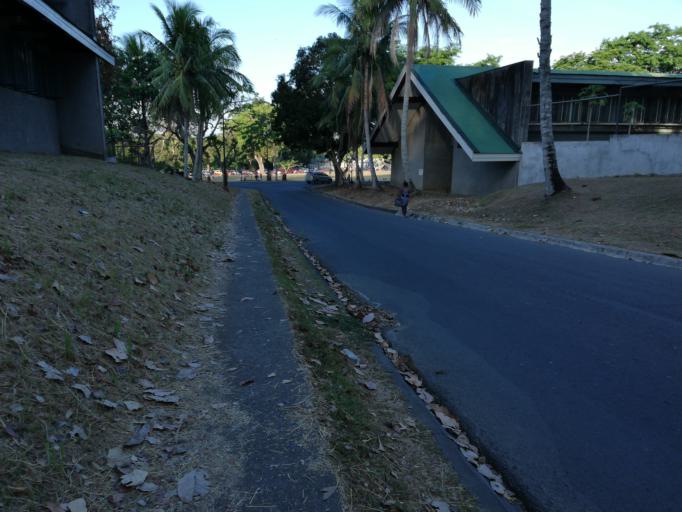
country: PH
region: Calabarzon
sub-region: Province of Laguna
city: Los Banos
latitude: 14.1617
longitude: 121.2402
